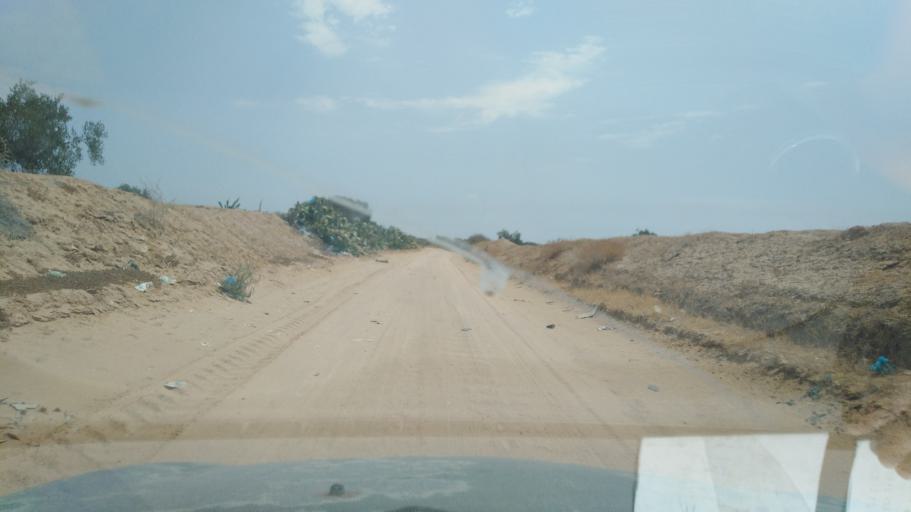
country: TN
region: Safaqis
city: Sfax
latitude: 34.7389
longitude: 10.5484
